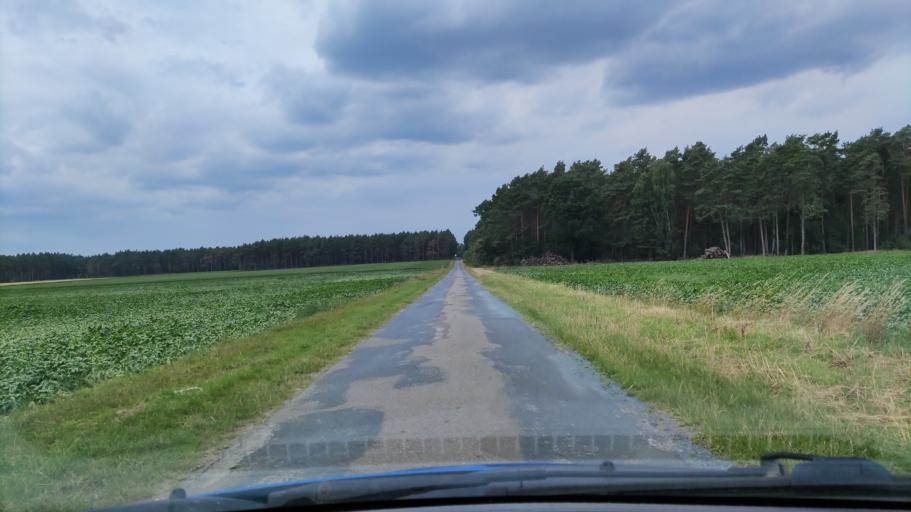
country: DE
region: Lower Saxony
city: Schnega
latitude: 52.9456
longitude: 10.8658
